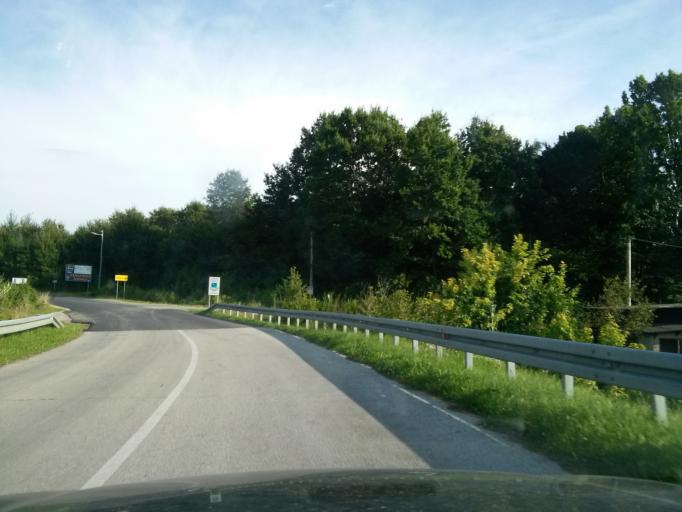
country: HR
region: Grad Zagreb
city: Horvati
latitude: 45.5468
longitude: 15.8573
